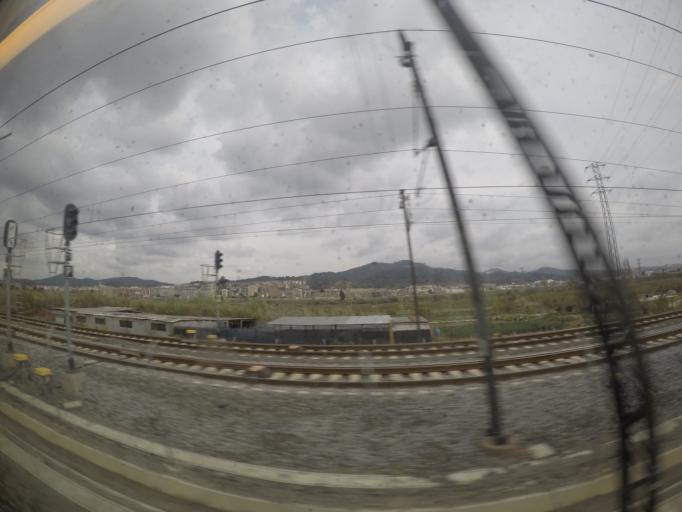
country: ES
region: Catalonia
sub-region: Provincia de Barcelona
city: Sant Vicenc dels Horts
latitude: 41.4019
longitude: 2.0139
